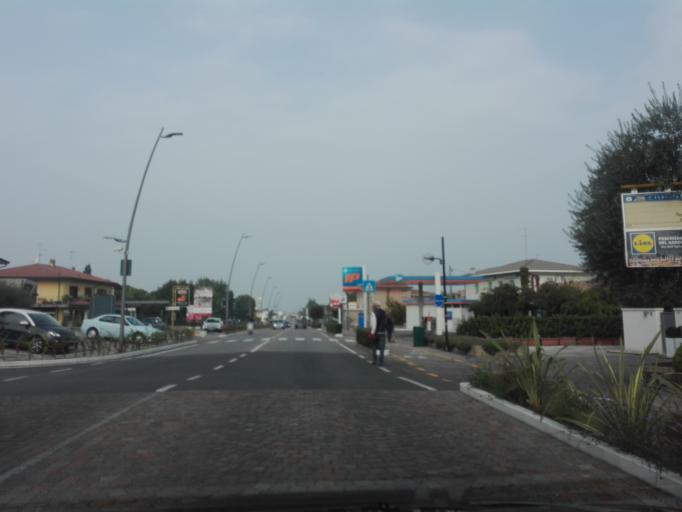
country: IT
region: Veneto
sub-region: Provincia di Verona
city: Peschiera del Garda
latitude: 45.4473
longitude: 10.6684
